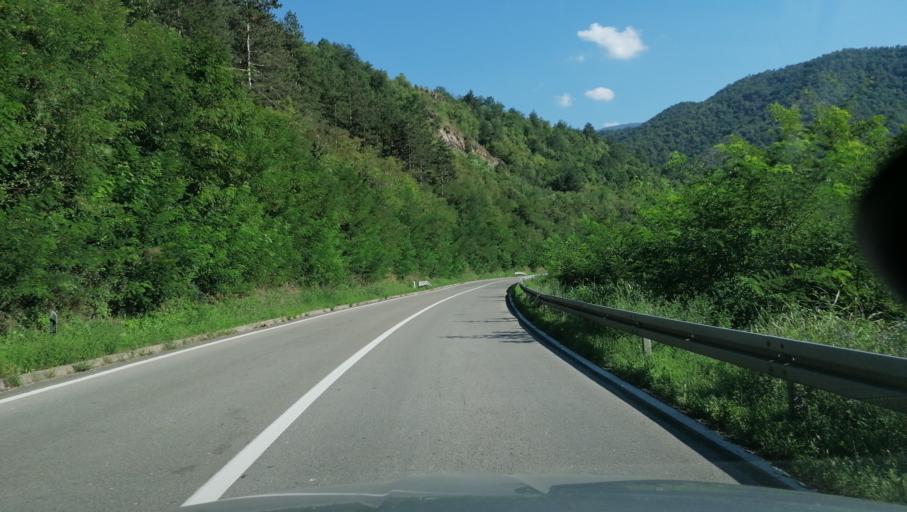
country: RS
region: Central Serbia
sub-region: Raski Okrug
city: Kraljevo
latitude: 43.6644
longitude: 20.5815
